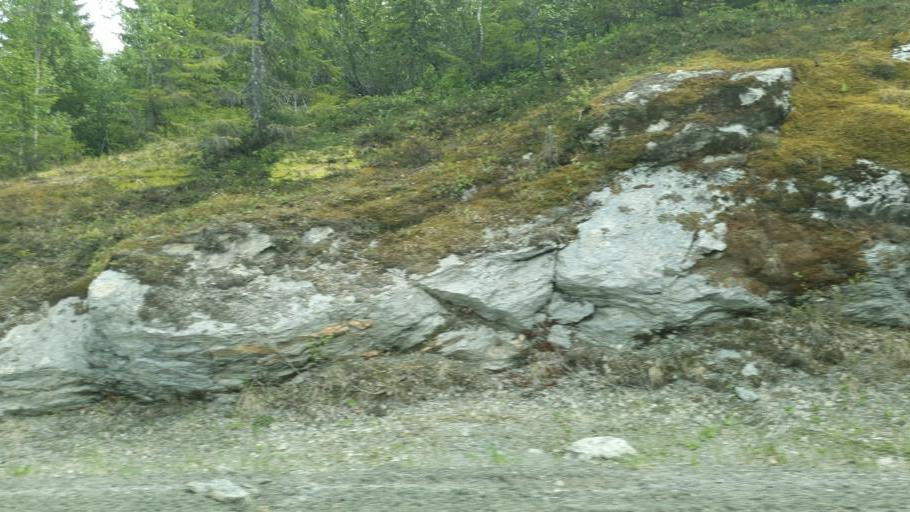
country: NO
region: Nord-Trondelag
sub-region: Leksvik
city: Leksvik
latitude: 63.6845
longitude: 10.3763
